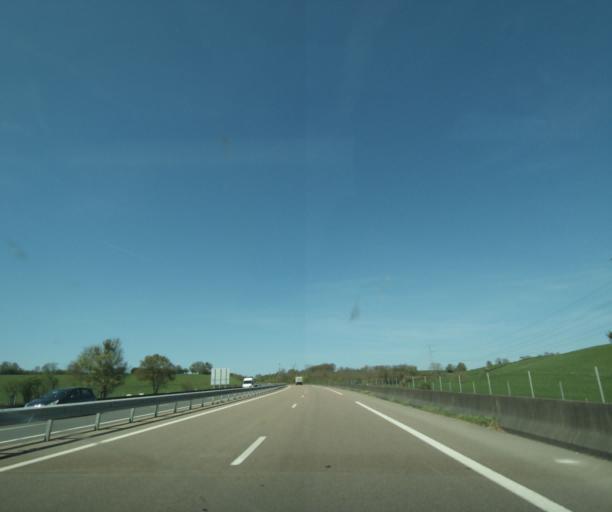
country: FR
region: Bourgogne
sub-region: Departement de la Nievre
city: Pougues-les-Eaux
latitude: 47.0800
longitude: 3.1230
